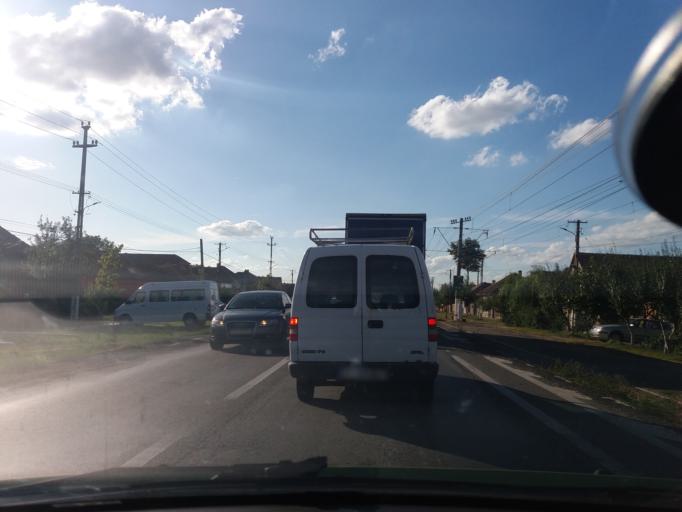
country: RO
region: Arad
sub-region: Comuna Vladimirescu
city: Vladimirescu
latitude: 46.1659
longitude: 21.3972
